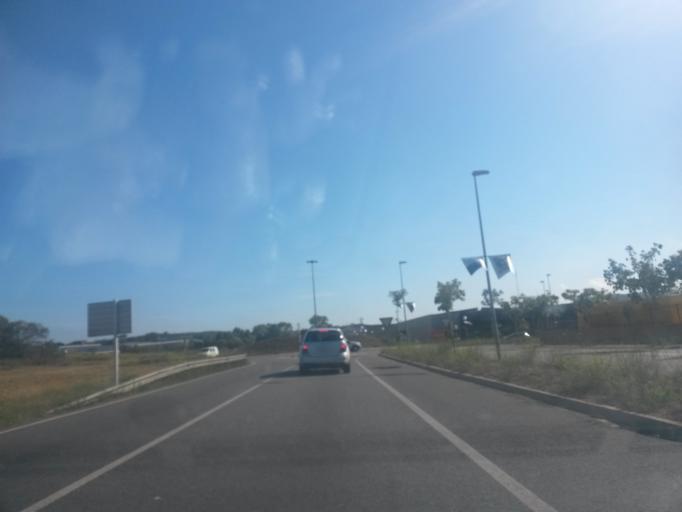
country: ES
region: Catalonia
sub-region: Provincia de Girona
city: Palafrugell
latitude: 41.9331
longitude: 3.1589
